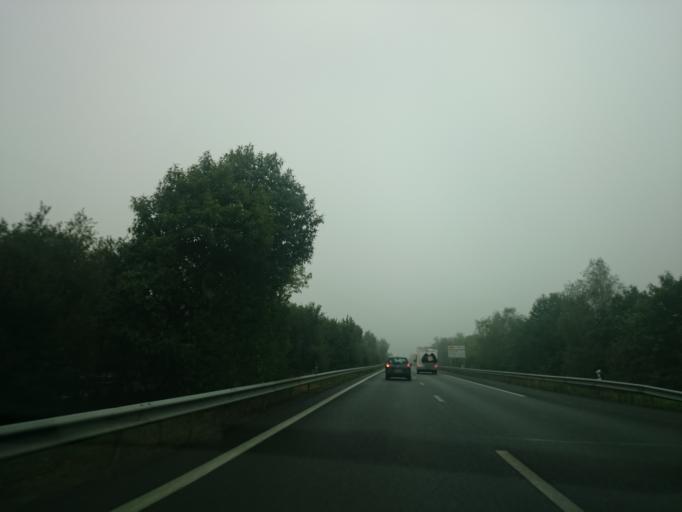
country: FR
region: Brittany
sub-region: Departement d'Ille-et-Vilaine
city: Crevin
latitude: 47.9510
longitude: -1.6791
